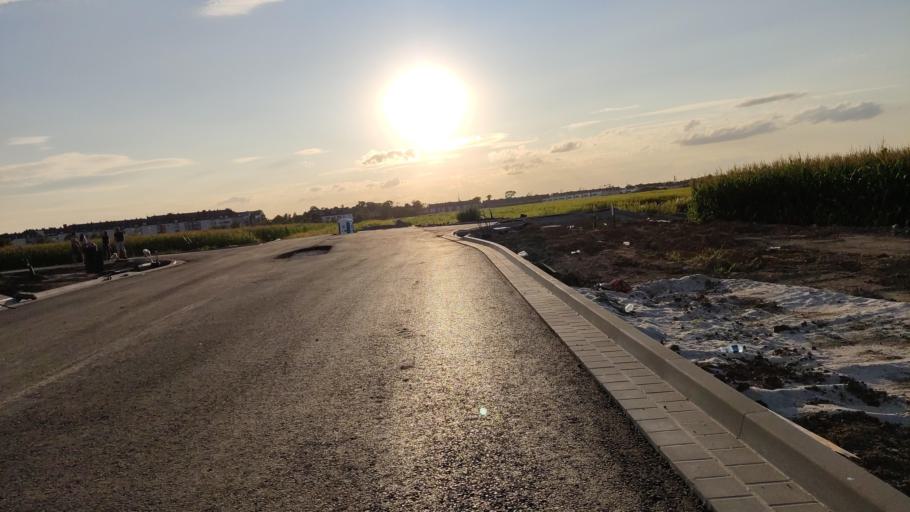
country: PL
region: Lower Silesian Voivodeship
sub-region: Powiat wroclawski
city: Zerniki Wroclawskie
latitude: 51.0630
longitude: 17.0525
